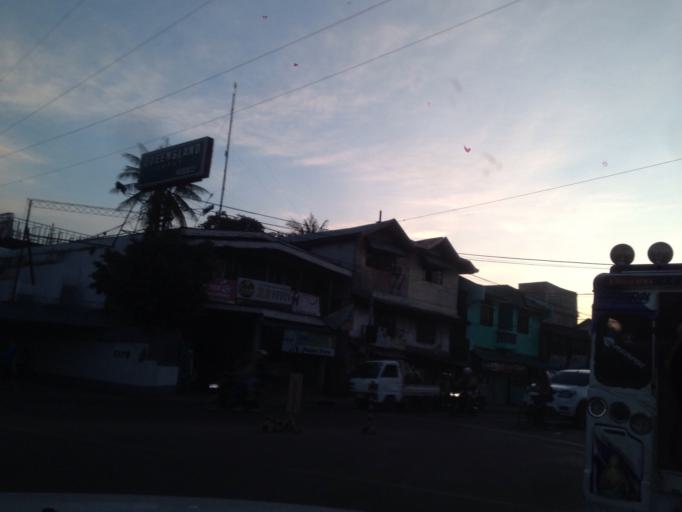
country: PH
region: Central Visayas
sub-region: Cebu City
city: Baugo
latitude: 10.3073
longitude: 123.9098
